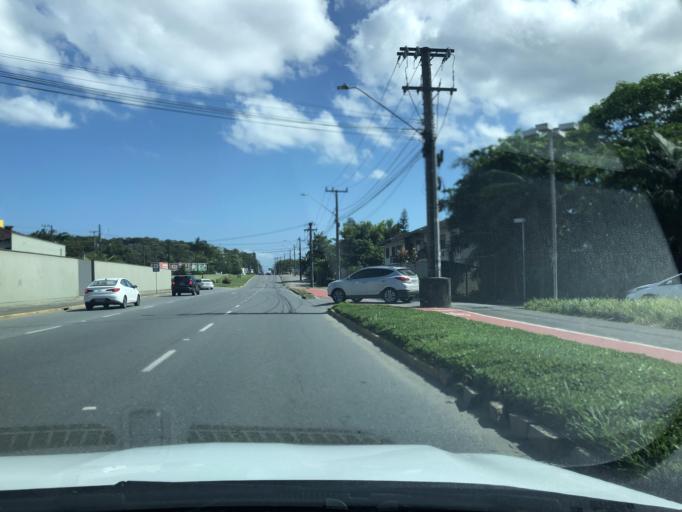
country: BR
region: Santa Catarina
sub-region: Joinville
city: Joinville
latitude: -26.2547
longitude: -48.8521
